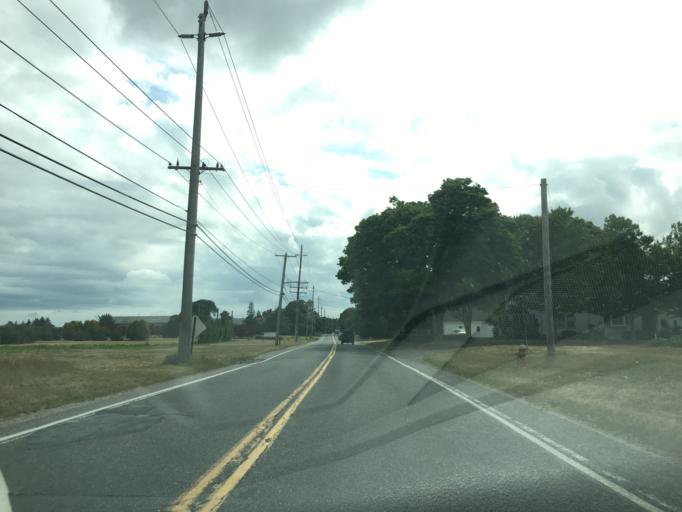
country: US
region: New York
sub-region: Suffolk County
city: Northville
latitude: 40.9812
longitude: -72.5973
